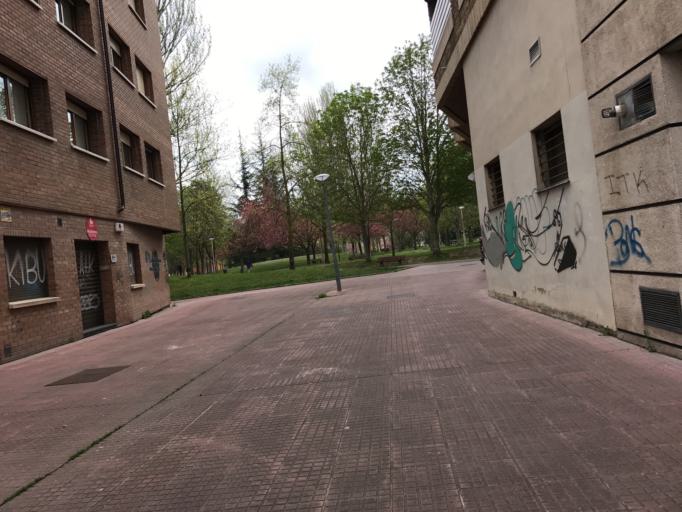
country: ES
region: Basque Country
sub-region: Provincia de Alava
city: Gasteiz / Vitoria
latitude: 42.8486
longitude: -2.6887
